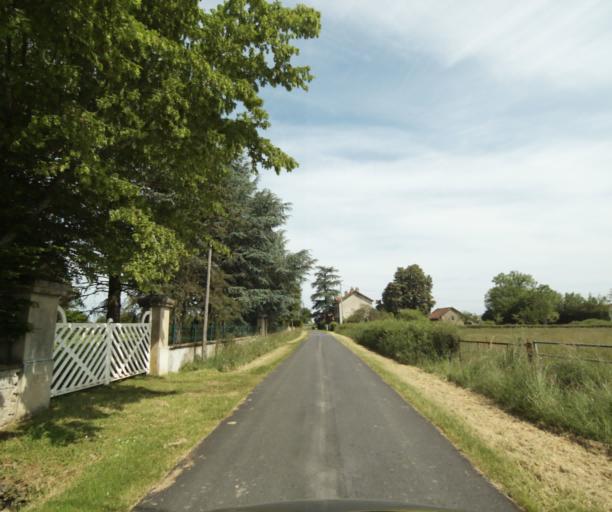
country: FR
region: Bourgogne
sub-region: Departement de Saone-et-Loire
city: Palinges
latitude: 46.5616
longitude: 4.1769
